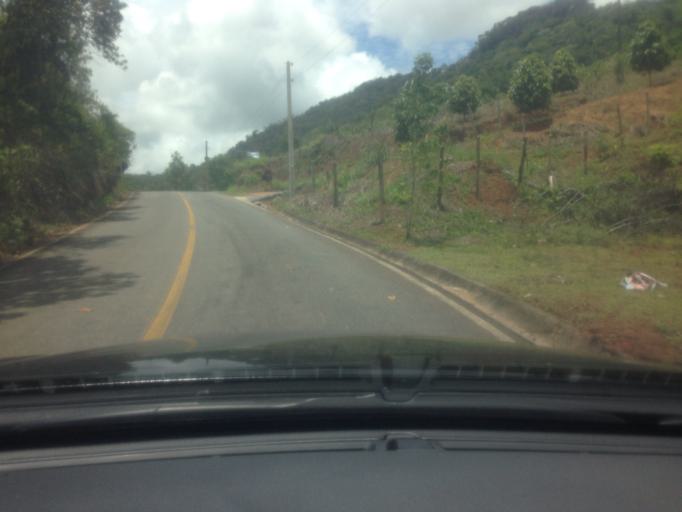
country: BR
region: Espirito Santo
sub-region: Guarapari
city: Guarapari
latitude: -20.5910
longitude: -40.5383
